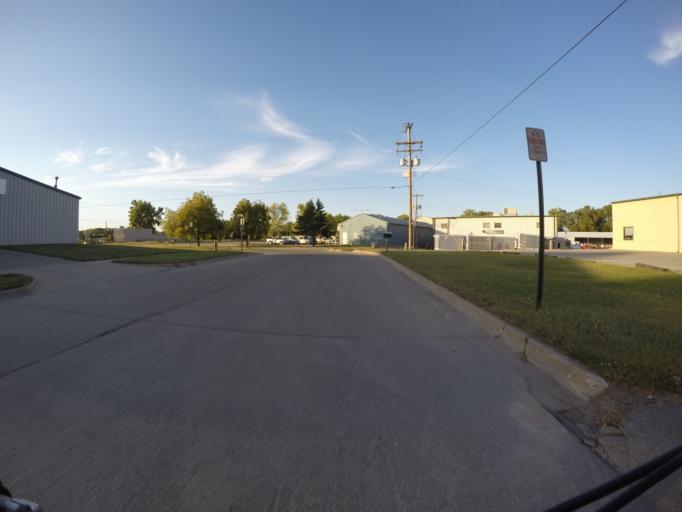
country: US
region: Kansas
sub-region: Riley County
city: Manhattan
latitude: 39.1671
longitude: -96.5943
